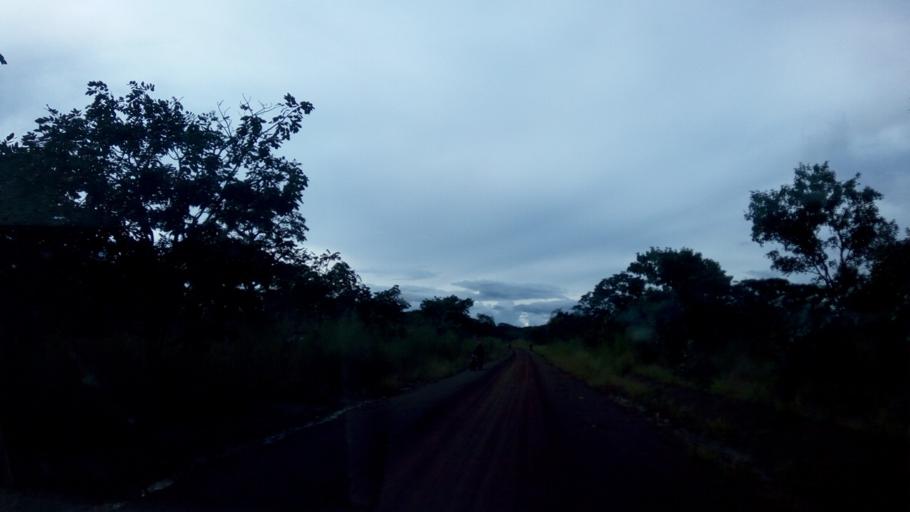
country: ZM
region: Luapula
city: Mwense
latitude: -10.4568
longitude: 28.1291
